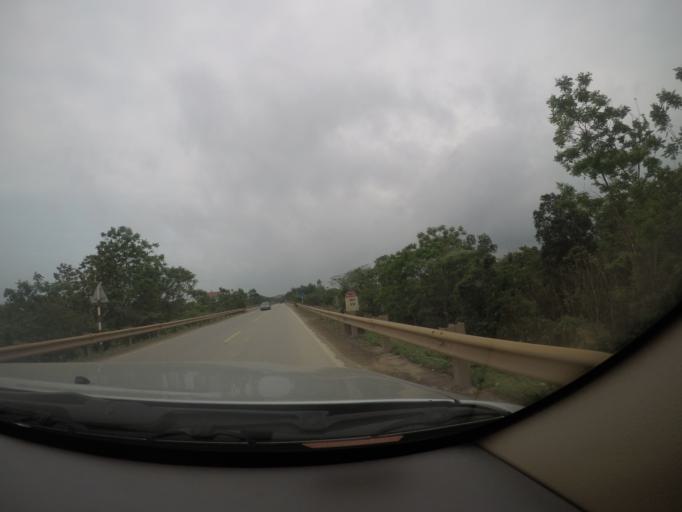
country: VN
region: Quang Binh
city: Kien Giang
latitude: 17.2324
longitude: 106.6969
